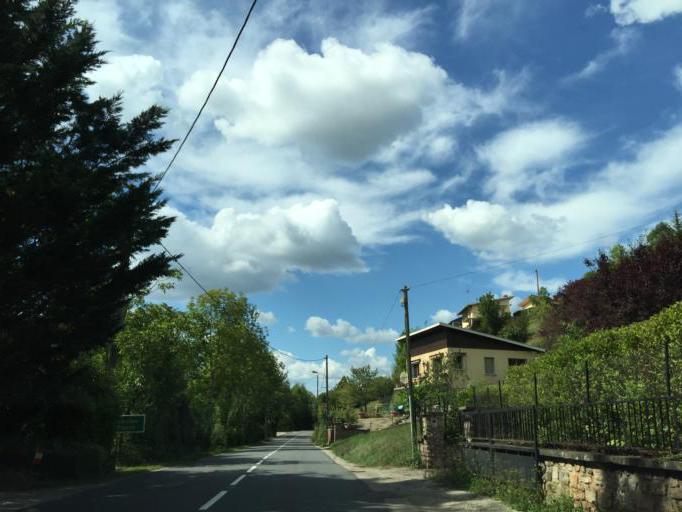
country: FR
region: Midi-Pyrenees
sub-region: Departement de l'Aveyron
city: Marcillac-Vallon
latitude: 44.4681
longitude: 2.4673
